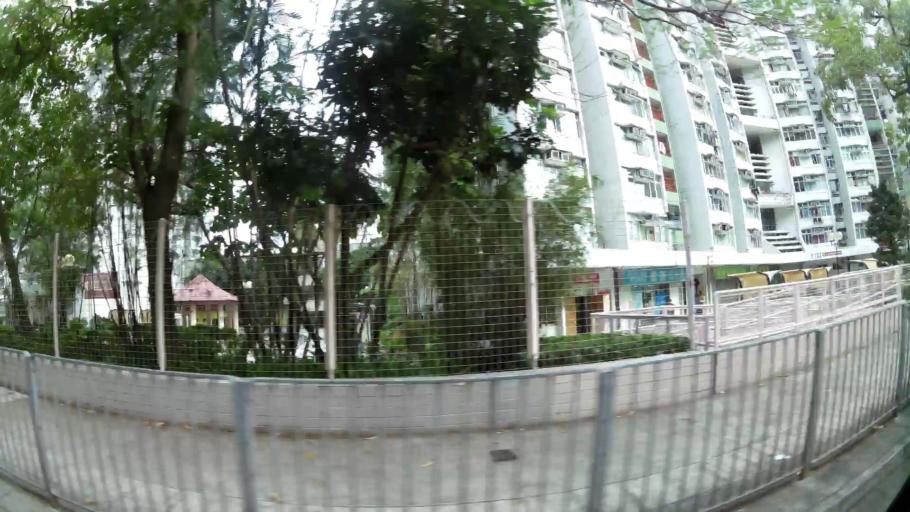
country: HK
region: Kowloon City
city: Kowloon
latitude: 22.3129
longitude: 114.2391
